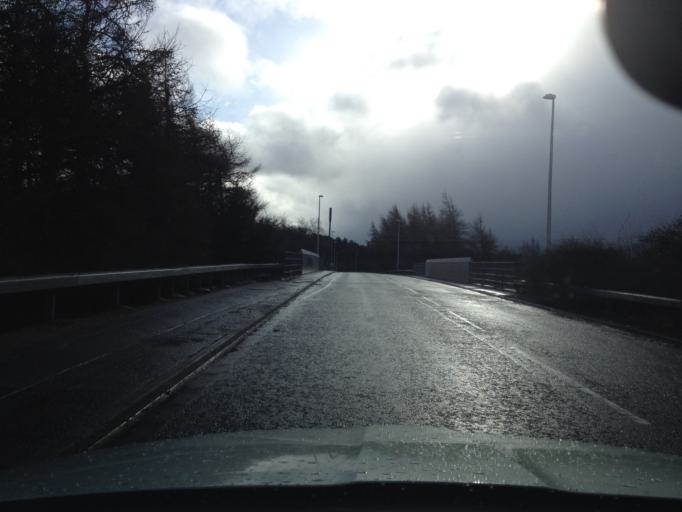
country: GB
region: Scotland
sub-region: West Lothian
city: Livingston
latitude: 55.9065
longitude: -3.5357
